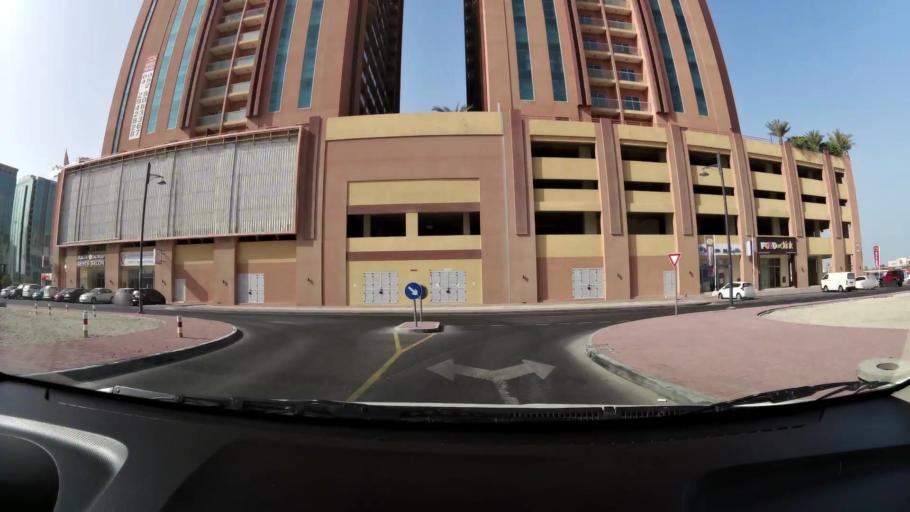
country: AE
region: Ash Shariqah
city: Sharjah
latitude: 25.2875
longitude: 55.3580
